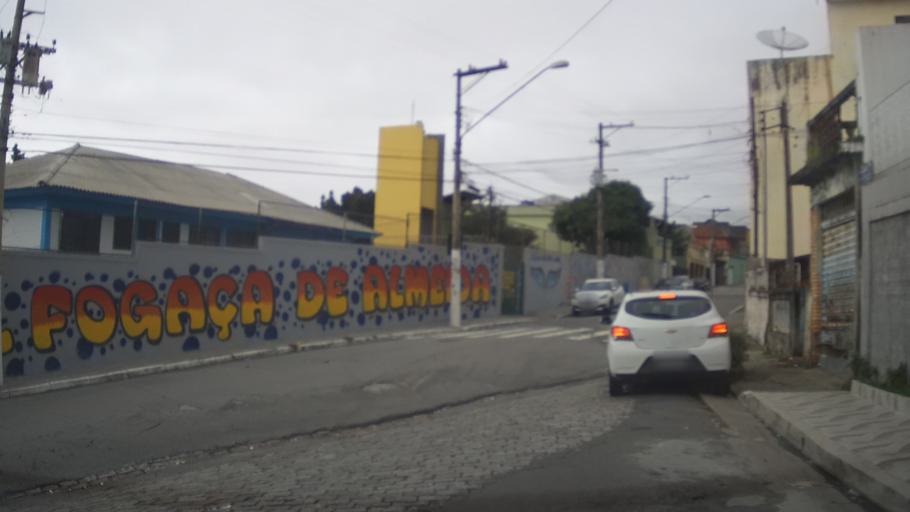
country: BR
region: Sao Paulo
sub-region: Guarulhos
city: Guarulhos
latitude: -23.5114
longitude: -46.5465
